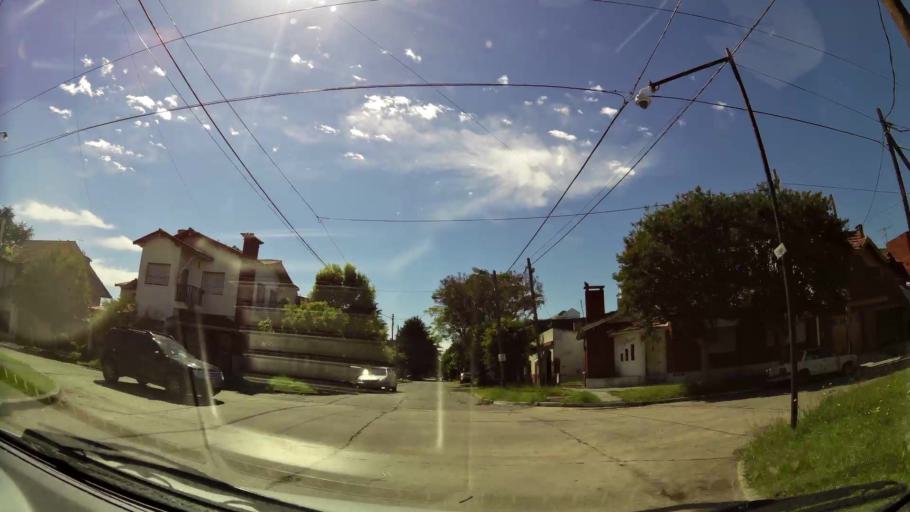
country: AR
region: Buenos Aires
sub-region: Partido de Quilmes
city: Quilmes
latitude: -34.6998
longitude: -58.3012
